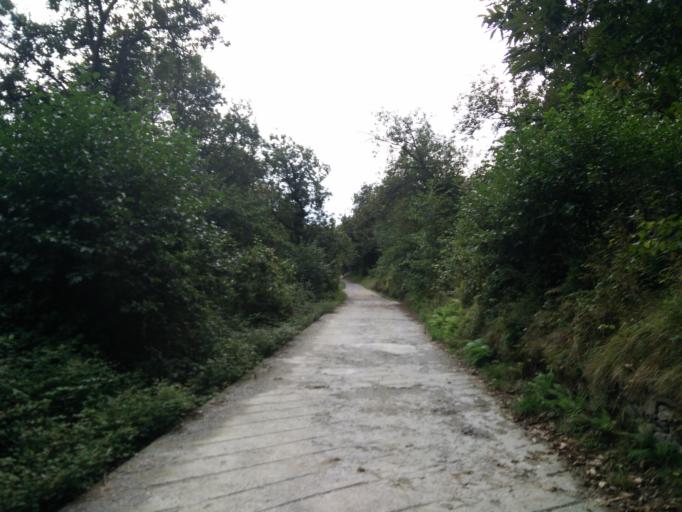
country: IT
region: Lombardy
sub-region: Provincia di Como
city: Livo
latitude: 46.1752
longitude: 9.3104
